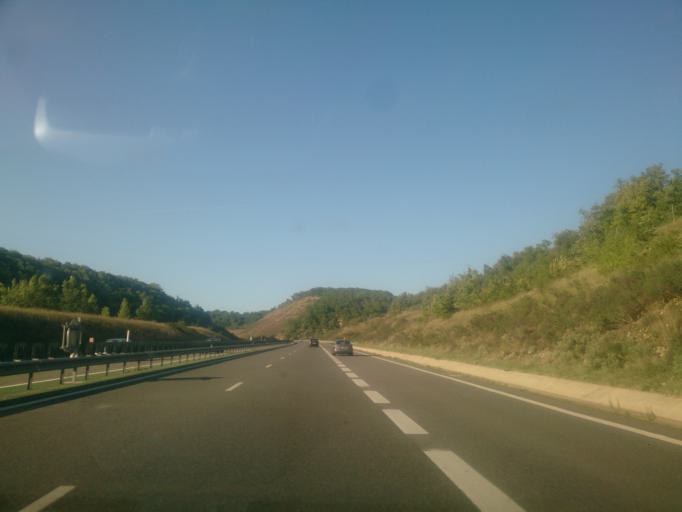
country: FR
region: Midi-Pyrenees
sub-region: Departement du Lot
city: Cahors
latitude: 44.4689
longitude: 1.5034
